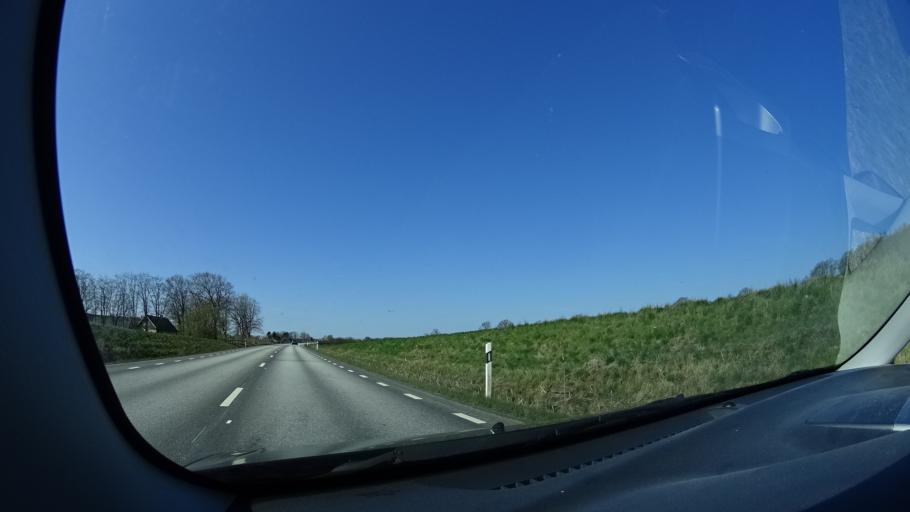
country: SE
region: Skane
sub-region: Hoganas Kommun
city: Hoganas
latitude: 56.2099
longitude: 12.6415
